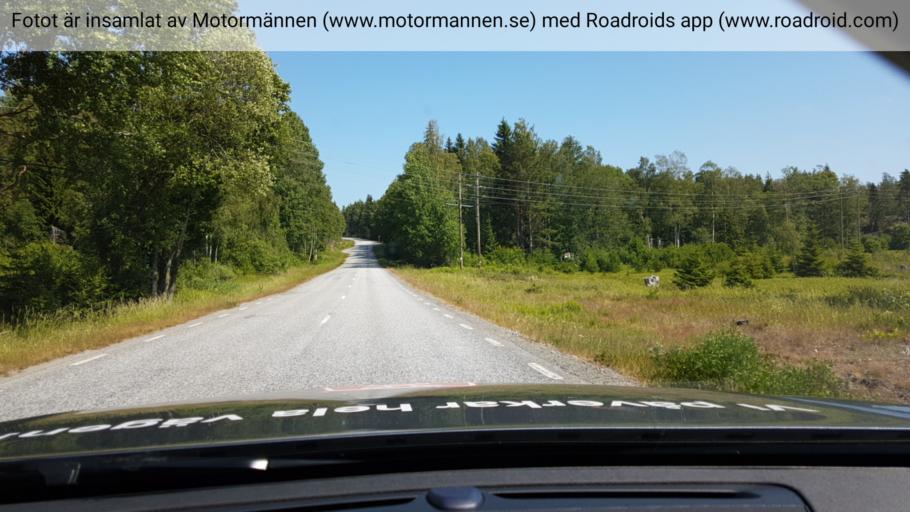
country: SE
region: Stockholm
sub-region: Haninge Kommun
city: Jordbro
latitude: 58.9880
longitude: 18.0965
